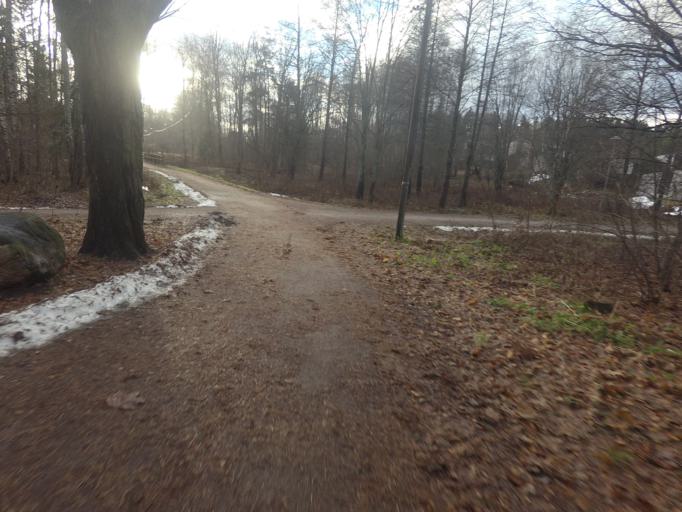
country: FI
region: Uusimaa
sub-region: Helsinki
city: Kilo
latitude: 60.1897
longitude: 24.7667
